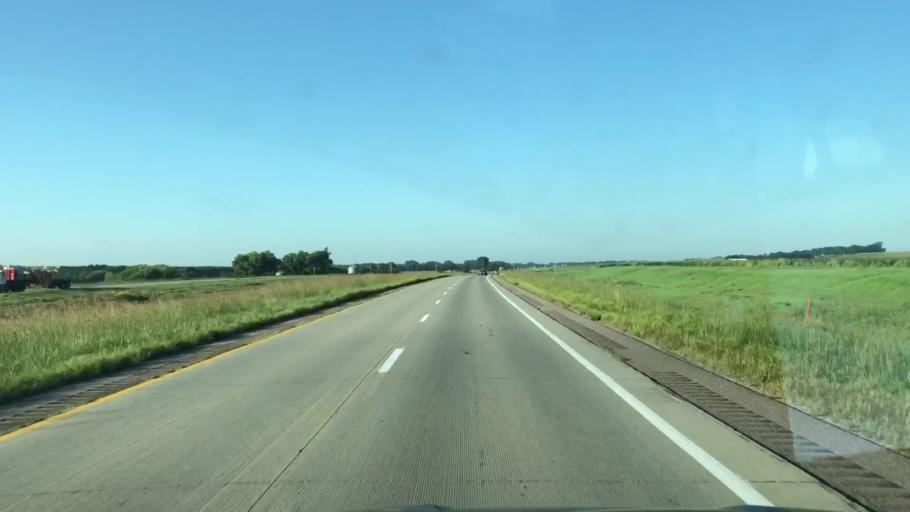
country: US
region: Iowa
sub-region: Plymouth County
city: Le Mars
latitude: 42.8858
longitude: -96.0968
